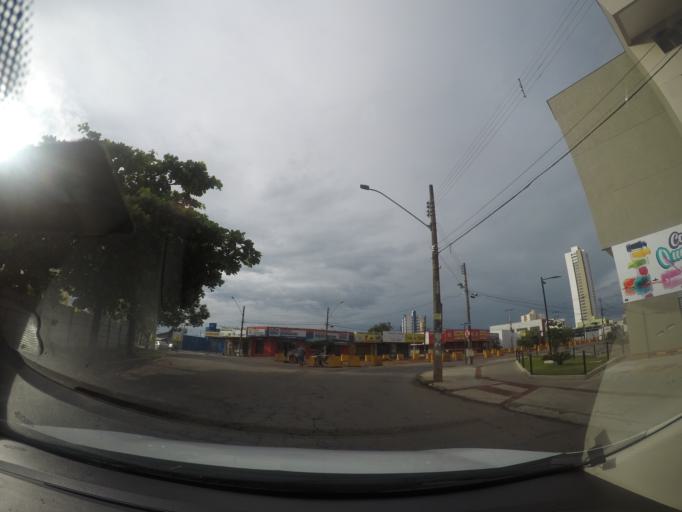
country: BR
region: Goias
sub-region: Goiania
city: Goiania
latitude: -16.7141
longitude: -49.2533
